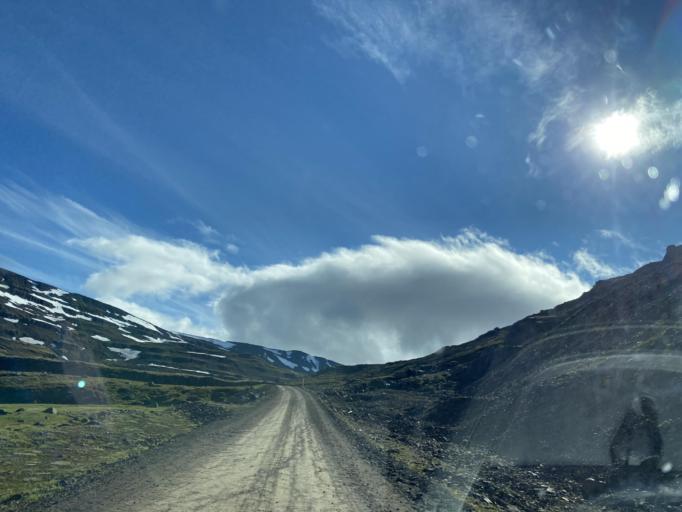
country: IS
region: East
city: Eskifjoerdur
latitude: 65.1738
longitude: -14.1159
